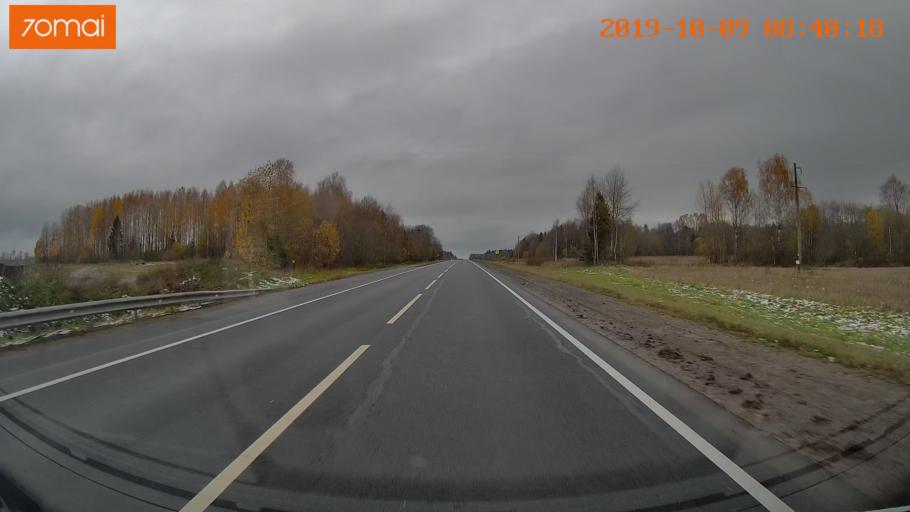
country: RU
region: Vologda
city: Gryazovets
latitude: 58.9844
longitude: 40.1422
